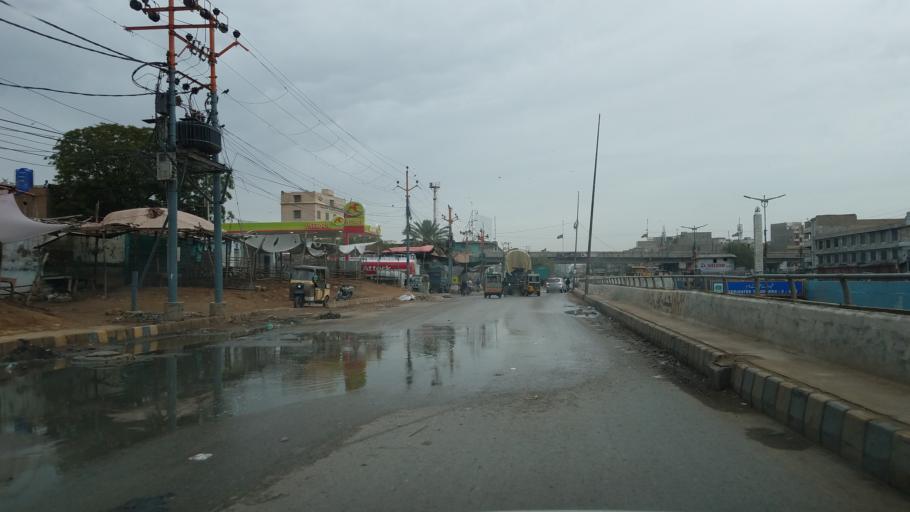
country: PK
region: Sindh
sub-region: Karachi District
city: Karachi
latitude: 24.9096
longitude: 67.0476
